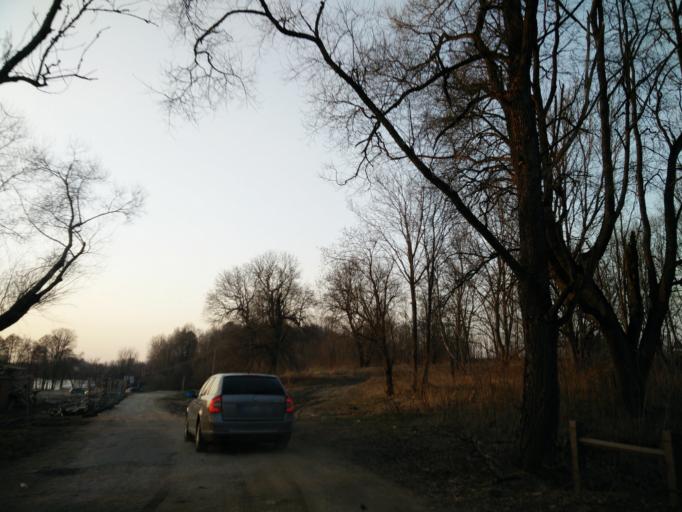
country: LT
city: Trakai
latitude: 54.6642
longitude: 24.9449
